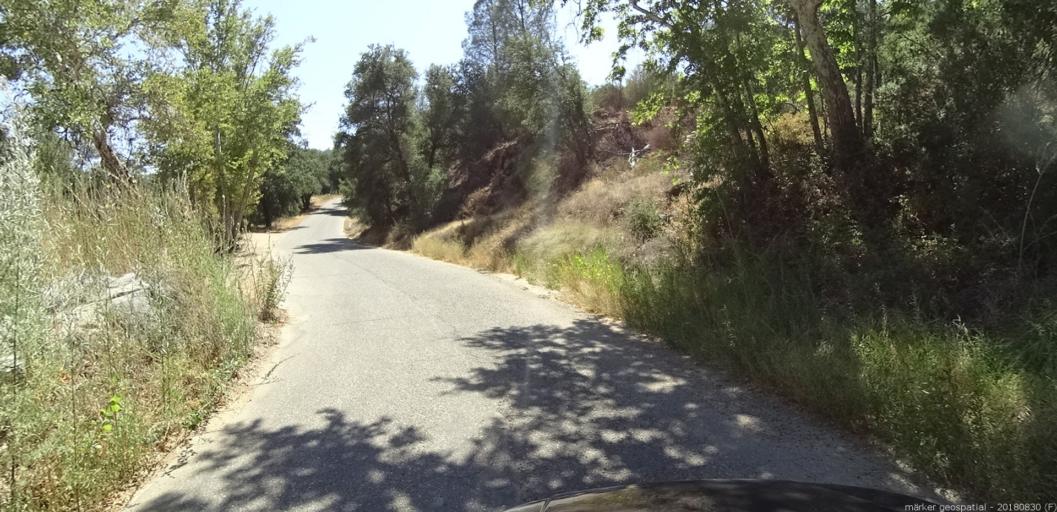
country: US
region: California
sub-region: Monterey County
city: King City
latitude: 36.0708
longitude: -121.3228
